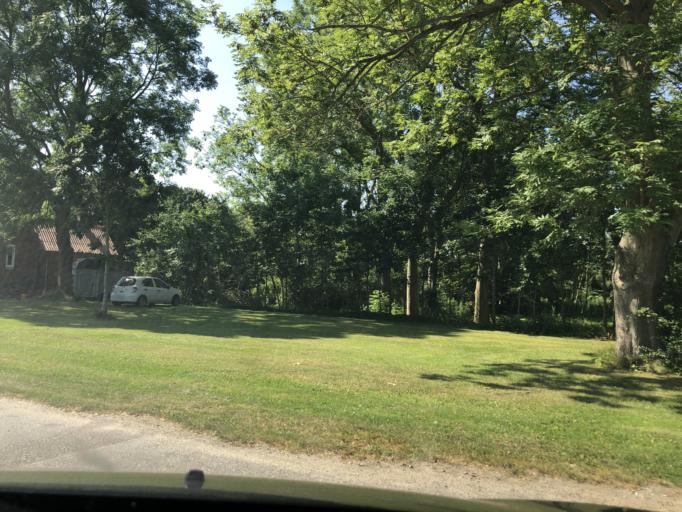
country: DK
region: South Denmark
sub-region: Faaborg-Midtfyn Kommune
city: Faaborg
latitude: 54.9557
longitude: 10.2242
